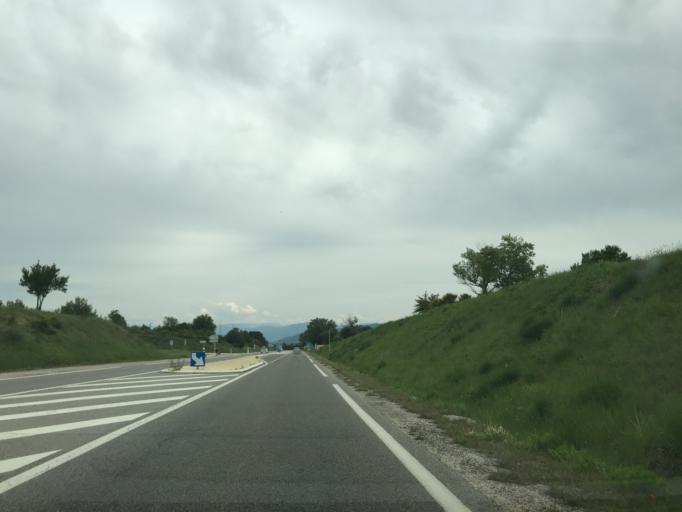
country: FR
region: Provence-Alpes-Cote d'Azur
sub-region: Departement des Alpes-de-Haute-Provence
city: Oraison
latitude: 43.9575
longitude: 5.8957
